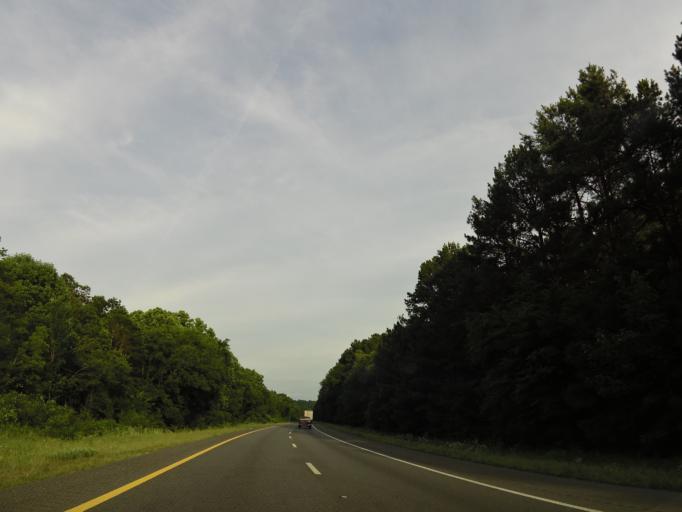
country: US
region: Tennessee
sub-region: Cheatham County
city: Pegram
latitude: 36.0866
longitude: -87.0517
